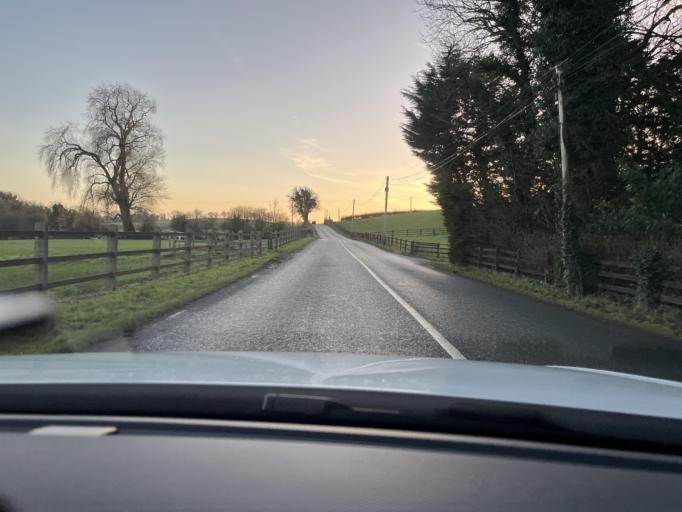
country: IE
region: Ulster
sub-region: An Cabhan
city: Ballyconnell
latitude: 54.0628
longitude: -7.6884
